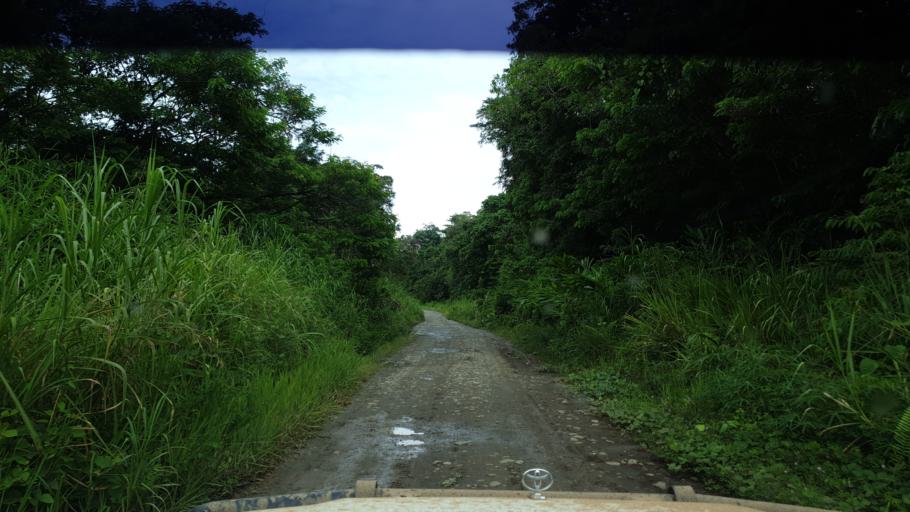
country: PG
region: Northern Province
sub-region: Sohe
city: Kokoda
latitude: -8.9163
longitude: 147.8550
